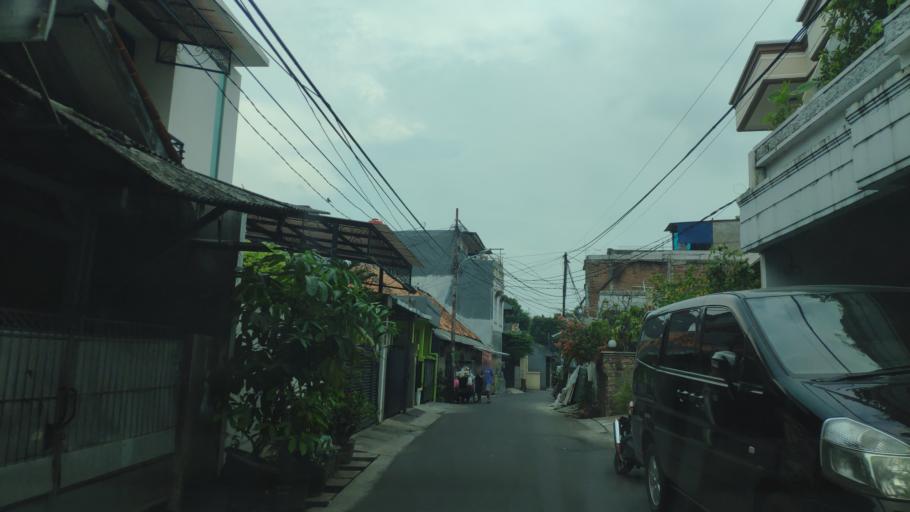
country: ID
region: Jakarta Raya
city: Jakarta
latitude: -6.1918
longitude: 106.8012
